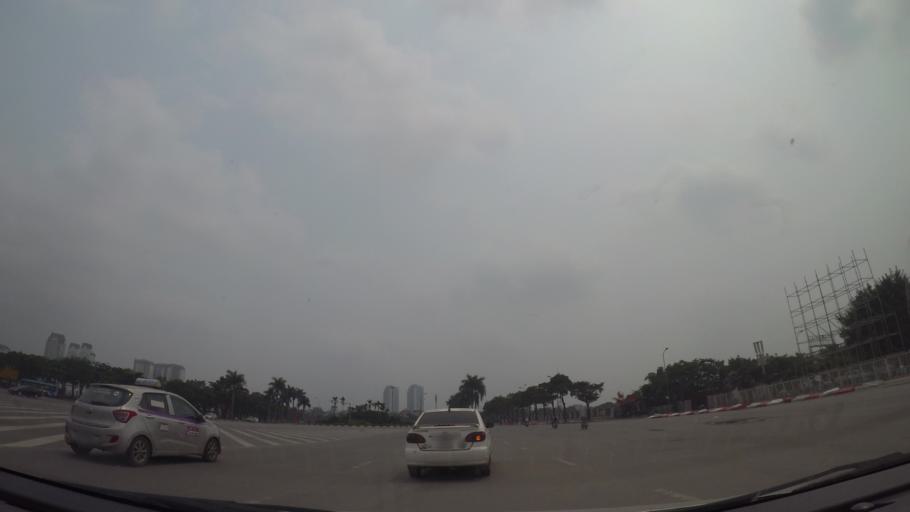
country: VN
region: Ha Noi
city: Cau Dien
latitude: 21.0197
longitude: 105.7662
